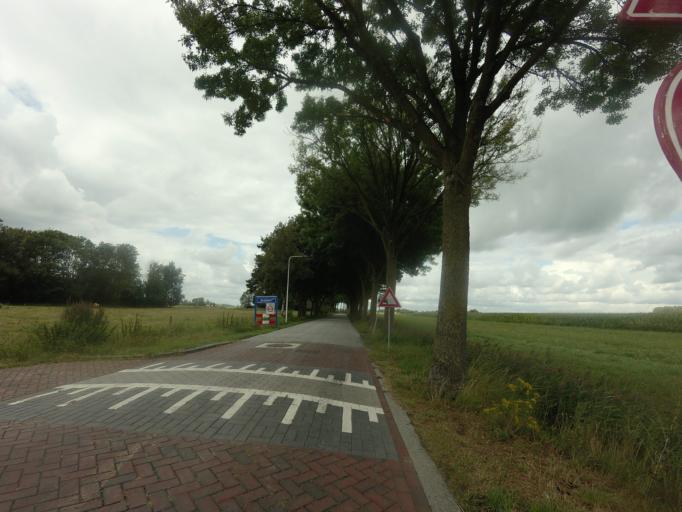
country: NL
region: Drenthe
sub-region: Gemeente Meppel
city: Meppel
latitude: 52.7097
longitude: 6.1783
